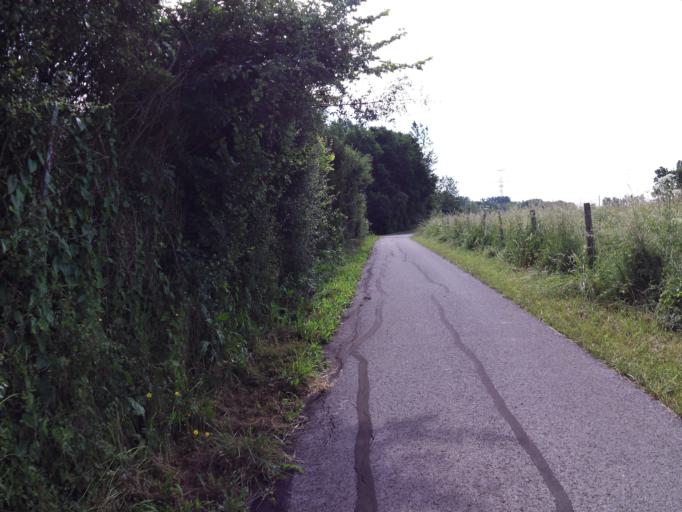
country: FR
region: Champagne-Ardenne
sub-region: Departement de l'Aube
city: Lusigny-sur-Barse
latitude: 48.2665
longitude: 4.2070
